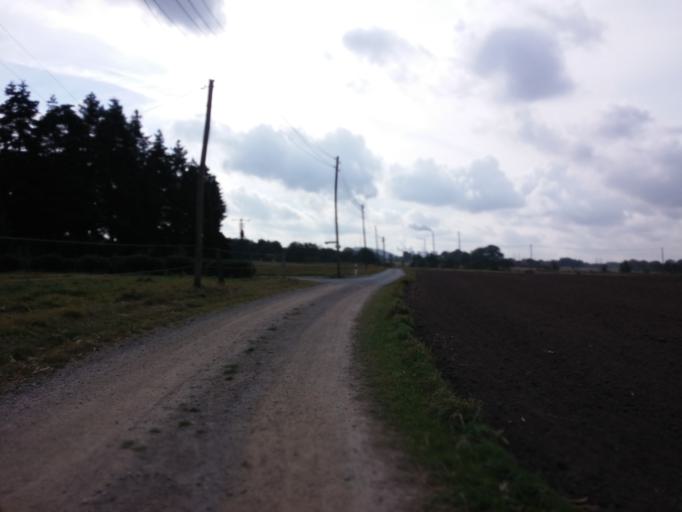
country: DE
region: North Rhine-Westphalia
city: Dorsten
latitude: 51.6481
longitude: 7.0149
